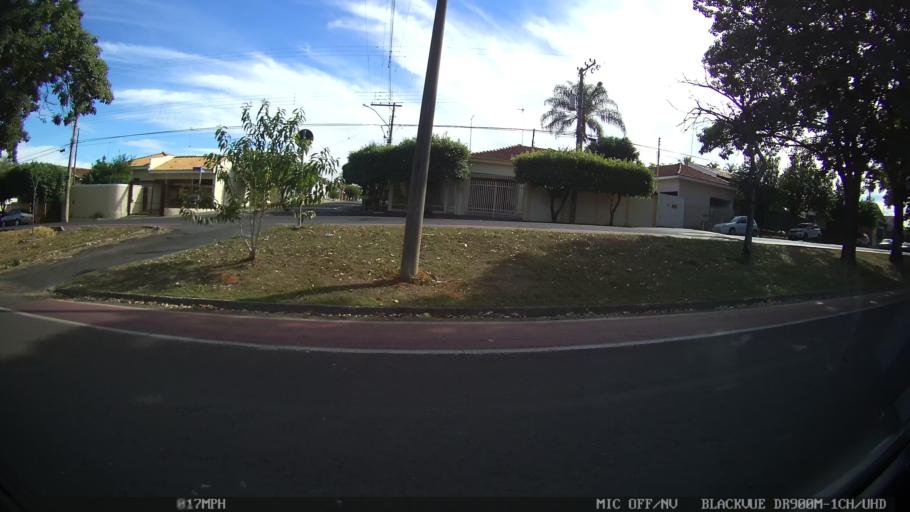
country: BR
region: Sao Paulo
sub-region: Catanduva
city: Catanduva
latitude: -21.1198
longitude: -48.9720
